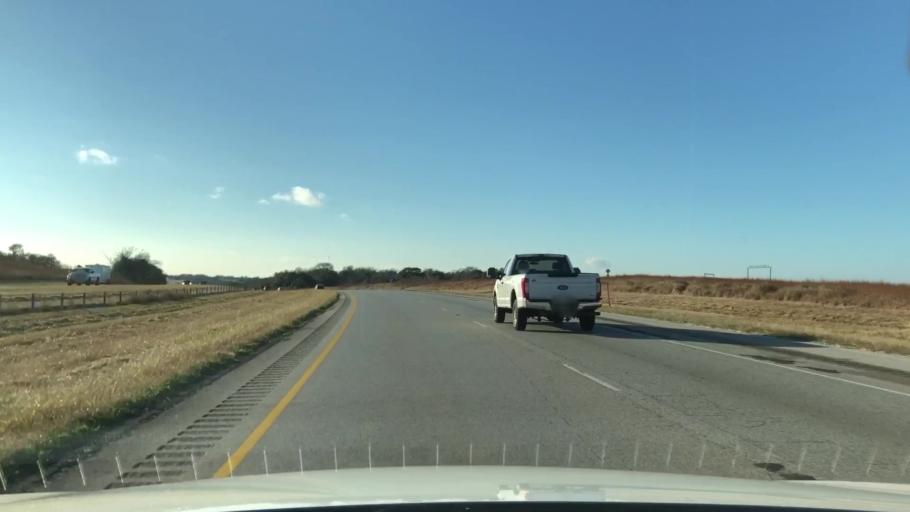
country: US
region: Texas
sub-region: Fayette County
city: Schulenburg
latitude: 29.6964
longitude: -96.8548
